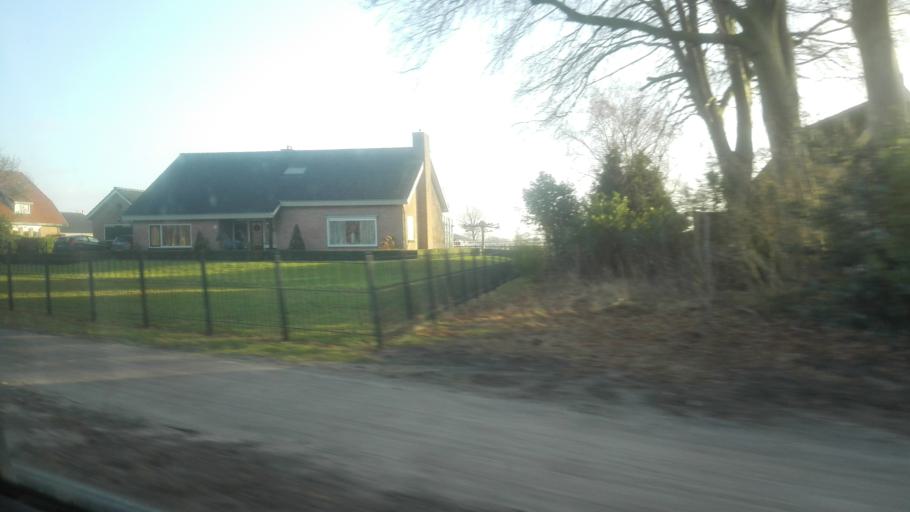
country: NL
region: Friesland
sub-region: Gemeente Heerenveen
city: Oudeschoot
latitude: 52.9329
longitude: 5.9734
